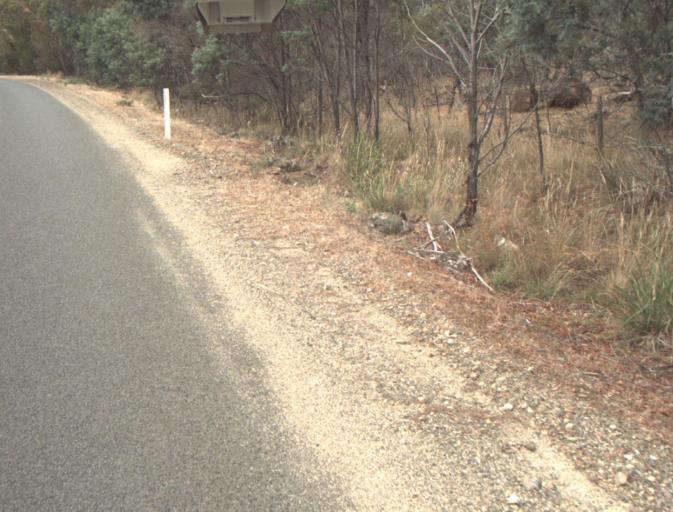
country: AU
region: Tasmania
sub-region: Northern Midlands
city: Evandale
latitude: -41.5068
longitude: 147.3559
